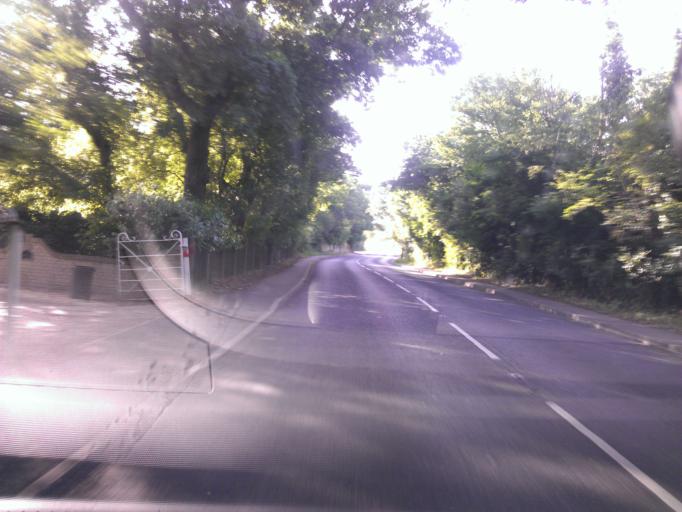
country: GB
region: England
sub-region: Essex
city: Little Clacton
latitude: 51.8379
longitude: 1.1323
